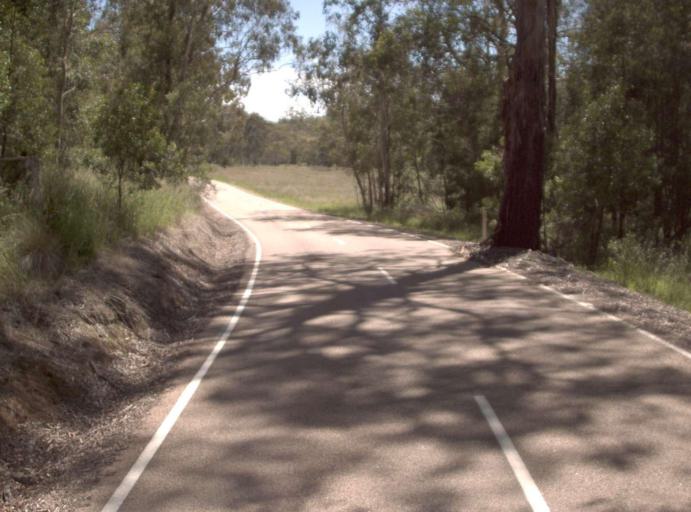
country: AU
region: Victoria
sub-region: East Gippsland
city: Lakes Entrance
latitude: -37.2355
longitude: 148.2590
